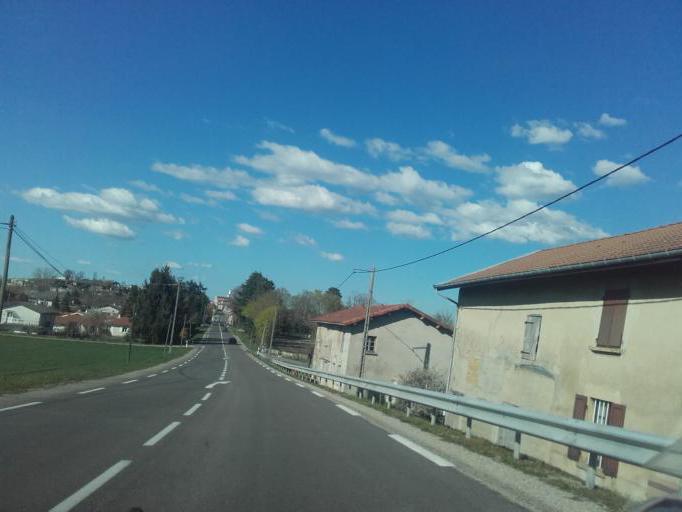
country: FR
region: Rhone-Alpes
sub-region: Departement de l'Isere
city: Champier
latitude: 45.4949
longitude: 5.2995
